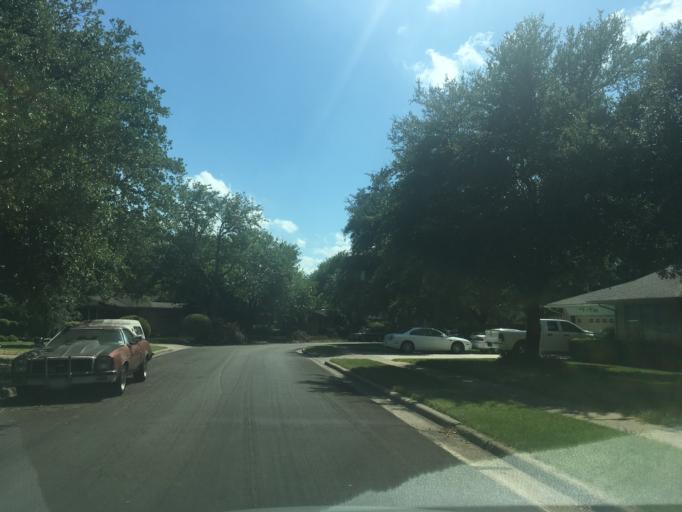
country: US
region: Texas
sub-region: Dallas County
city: Garland
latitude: 32.8320
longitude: -96.6808
